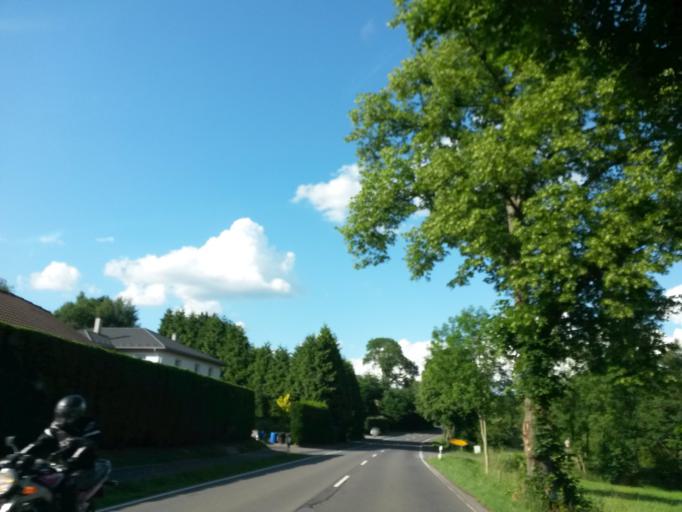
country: DE
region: North Rhine-Westphalia
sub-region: Regierungsbezirk Koln
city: Much
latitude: 50.9165
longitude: 7.4306
